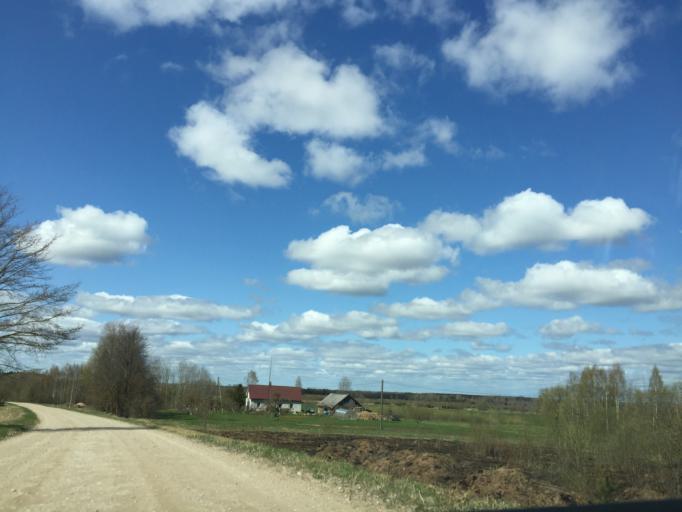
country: LV
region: Rezekne
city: Rezekne
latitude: 56.6430
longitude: 27.1574
